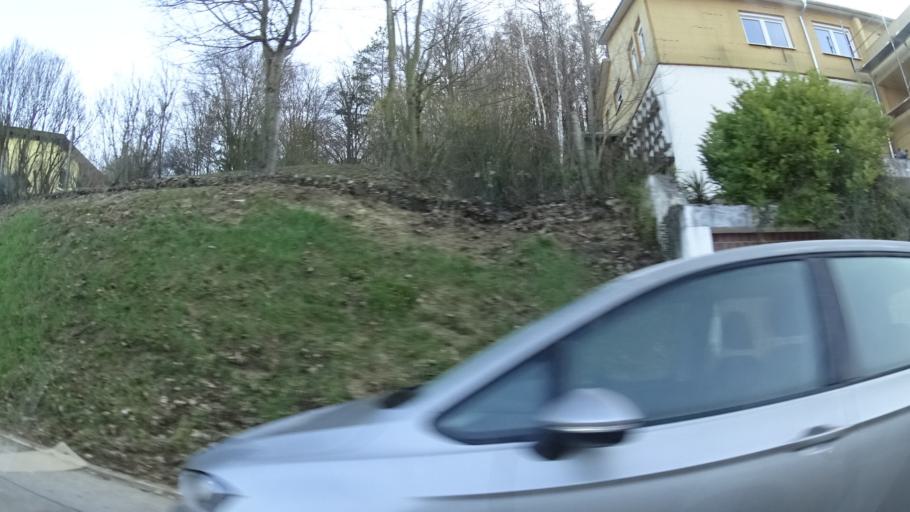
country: DE
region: Baden-Wuerttemberg
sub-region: Karlsruhe Region
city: Mosbach
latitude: 49.3436
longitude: 9.1382
